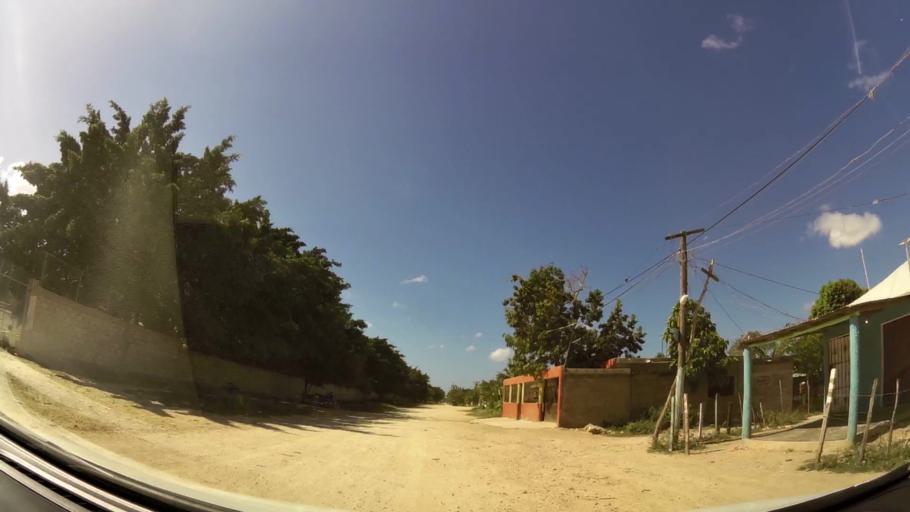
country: DO
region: Santo Domingo
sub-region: Santo Domingo
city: Boca Chica
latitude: 18.4605
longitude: -69.6242
